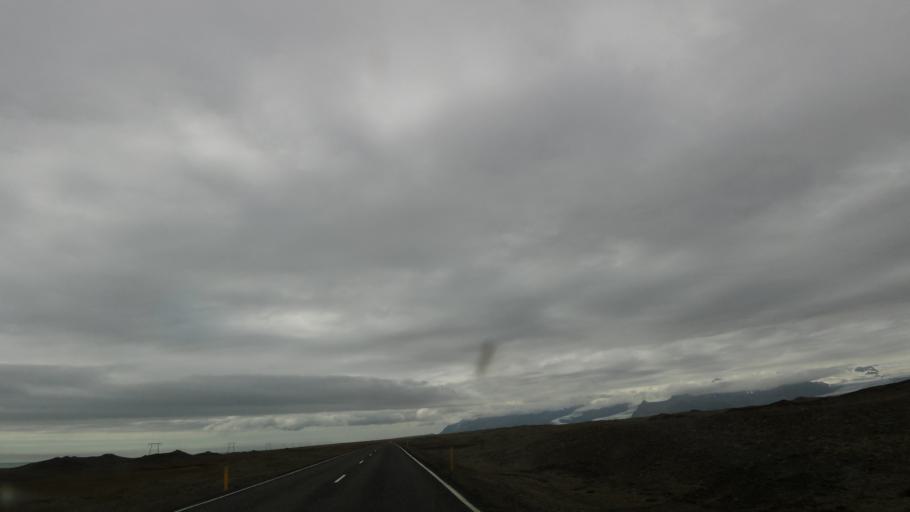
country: IS
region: East
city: Hoefn
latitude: 64.0745
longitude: -16.1153
